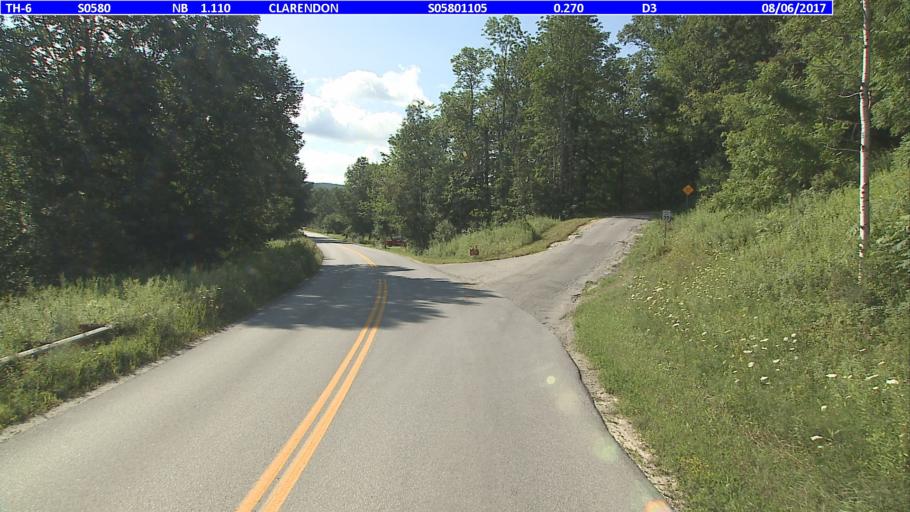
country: US
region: Vermont
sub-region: Rutland County
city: Rutland
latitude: 43.5704
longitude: -72.9508
